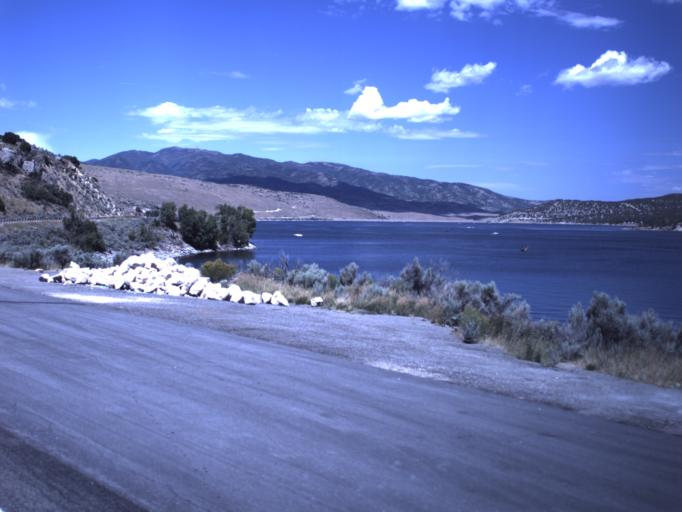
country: US
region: Utah
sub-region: Summit County
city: Oakley
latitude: 40.7575
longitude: -111.3896
